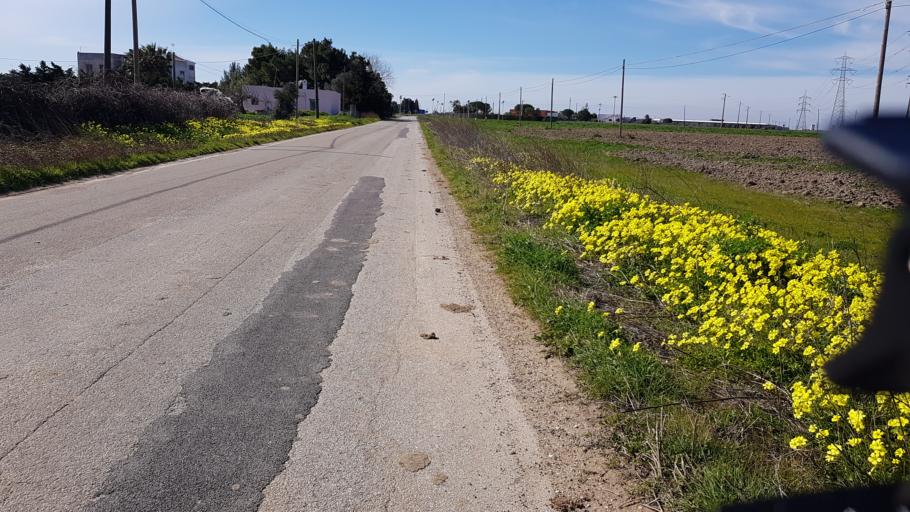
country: IT
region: Apulia
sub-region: Provincia di Brindisi
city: La Rosa
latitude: 40.5919
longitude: 17.9479
